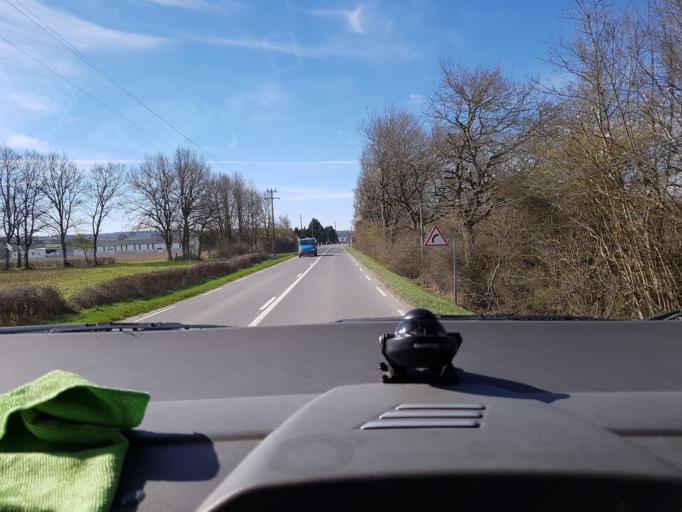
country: FR
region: Bourgogne
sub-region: Departement de Saone-et-Loire
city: Gueugnon
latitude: 46.5755
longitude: 4.0594
